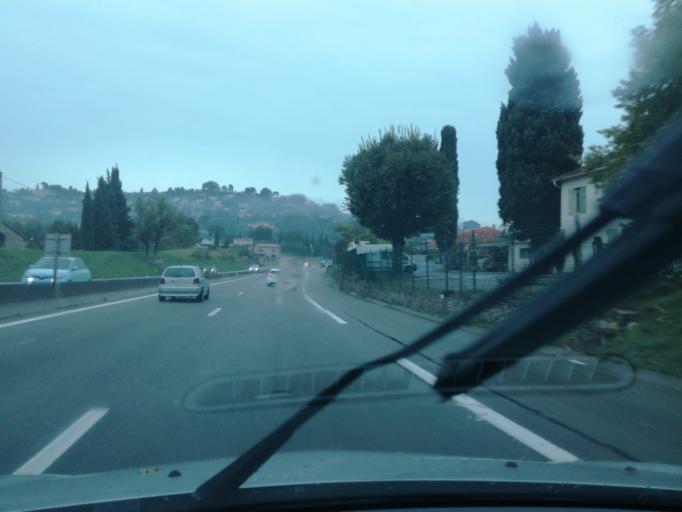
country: FR
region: Provence-Alpes-Cote d'Azur
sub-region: Departement des Alpes-Maritimes
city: Mougins
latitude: 43.5905
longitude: 7.0011
